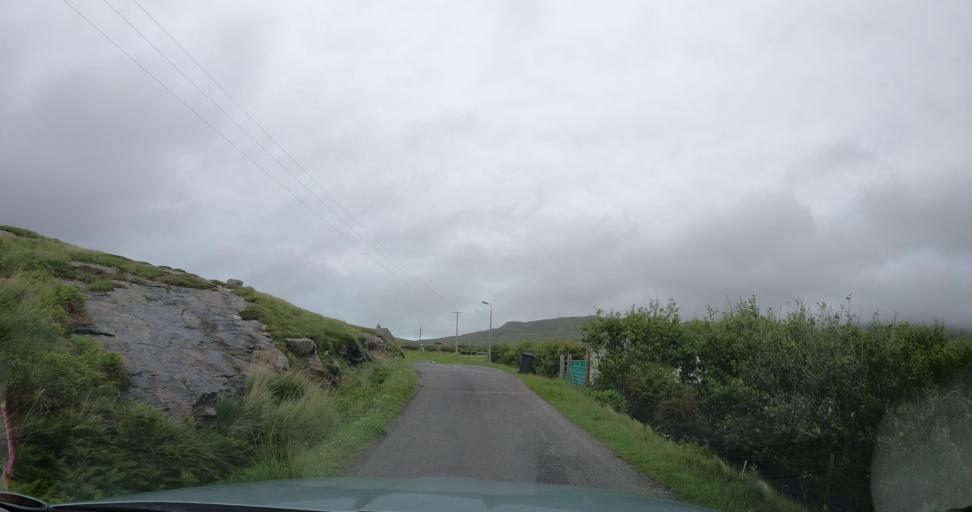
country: GB
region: Scotland
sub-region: Eilean Siar
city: Barra
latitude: 56.9554
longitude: -7.5070
